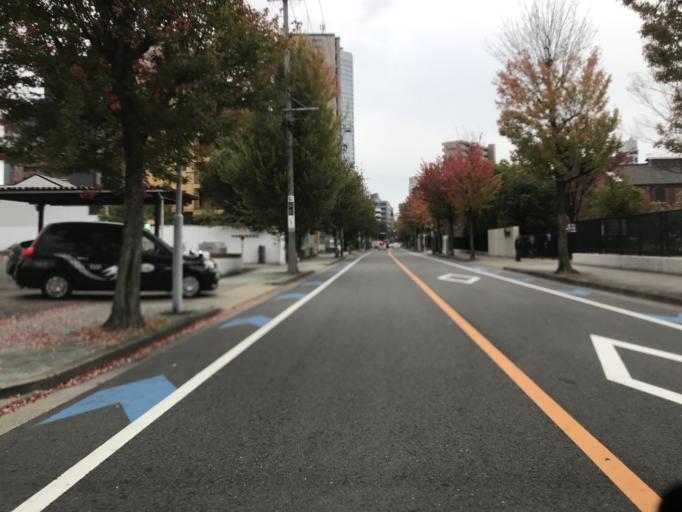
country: JP
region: Aichi
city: Nagoya-shi
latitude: 35.1794
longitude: 136.8819
